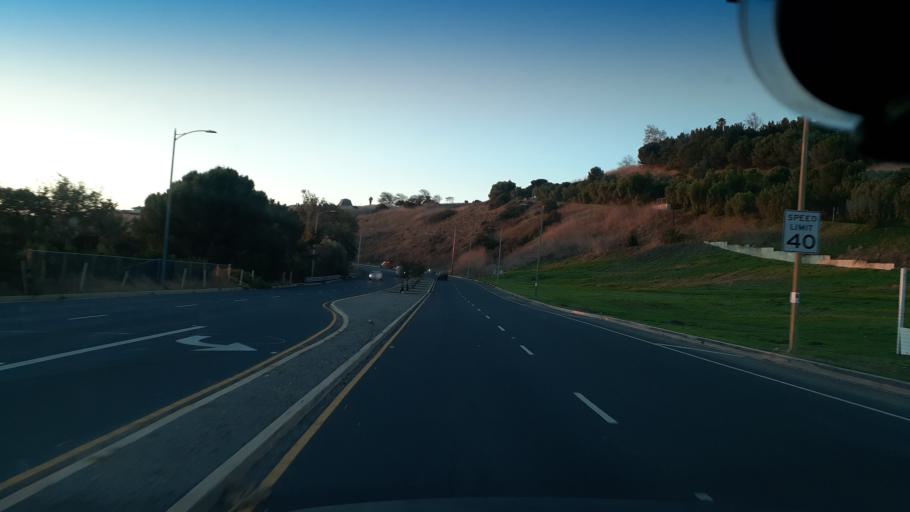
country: US
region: California
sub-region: Los Angeles County
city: San Pedro
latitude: 33.7359
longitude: -118.3167
